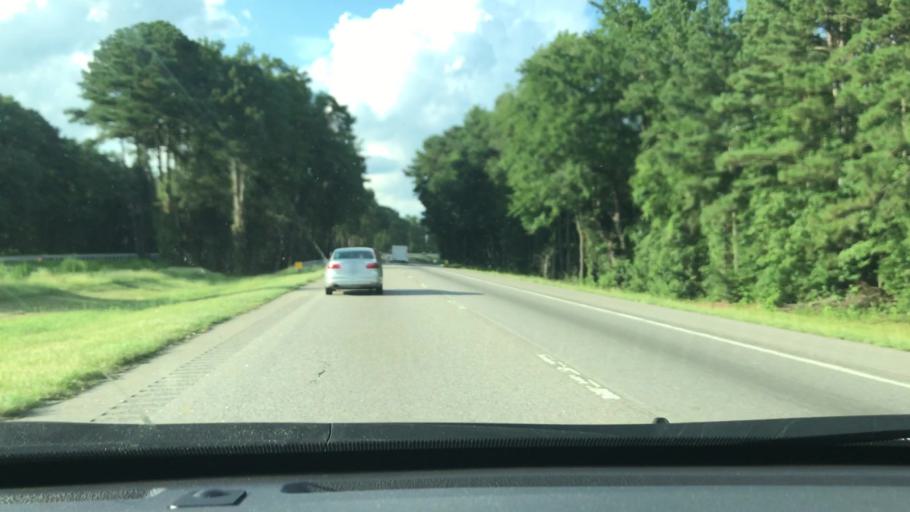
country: US
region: North Carolina
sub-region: Robeson County
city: Saint Pauls
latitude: 34.8255
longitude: -78.9827
